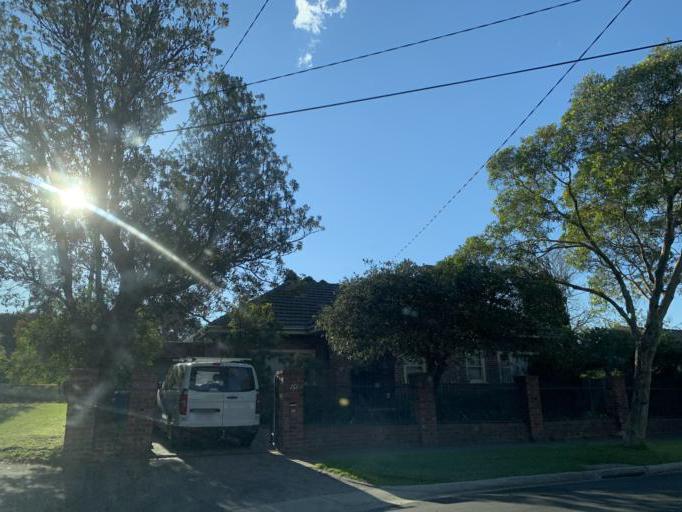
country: AU
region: Victoria
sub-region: Bayside
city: Hampton
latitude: -37.9440
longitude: 145.0062
